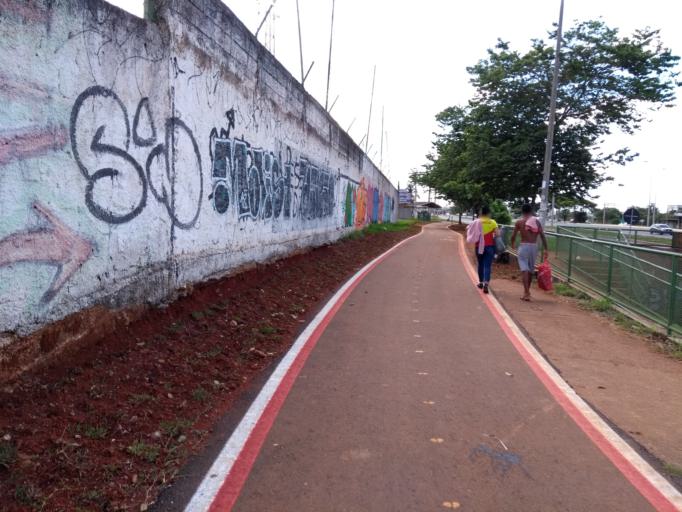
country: BR
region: Federal District
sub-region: Brasilia
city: Brasilia
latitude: -15.8121
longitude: -47.9882
